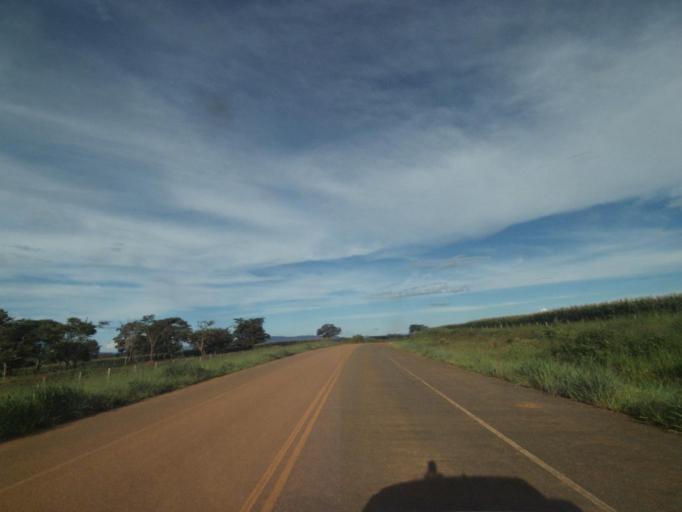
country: BR
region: Goias
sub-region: Jaragua
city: Jaragua
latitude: -15.8904
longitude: -49.4823
